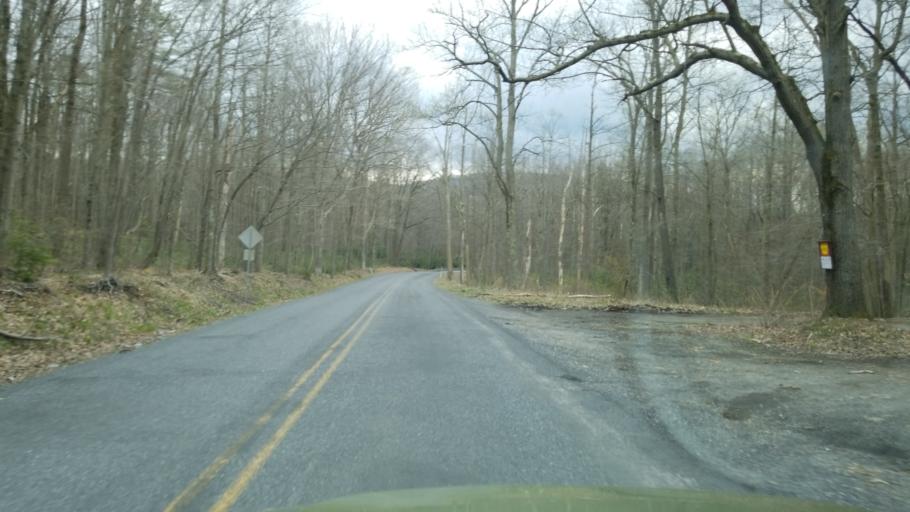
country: US
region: Pennsylvania
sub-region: Blair County
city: Tipton
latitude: 40.6852
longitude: -78.3302
